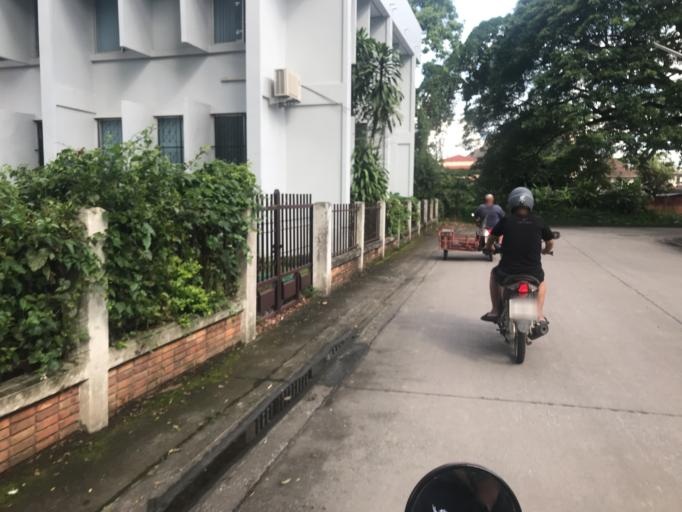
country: TH
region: Chiang Rai
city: Chiang Rai
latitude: 19.9141
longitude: 99.8314
